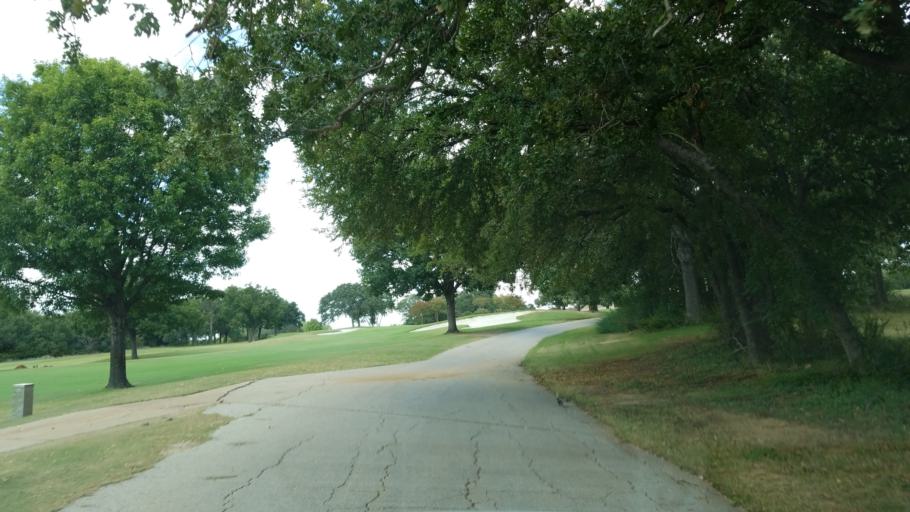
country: US
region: Texas
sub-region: Tarrant County
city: Euless
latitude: 32.8607
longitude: -97.0600
